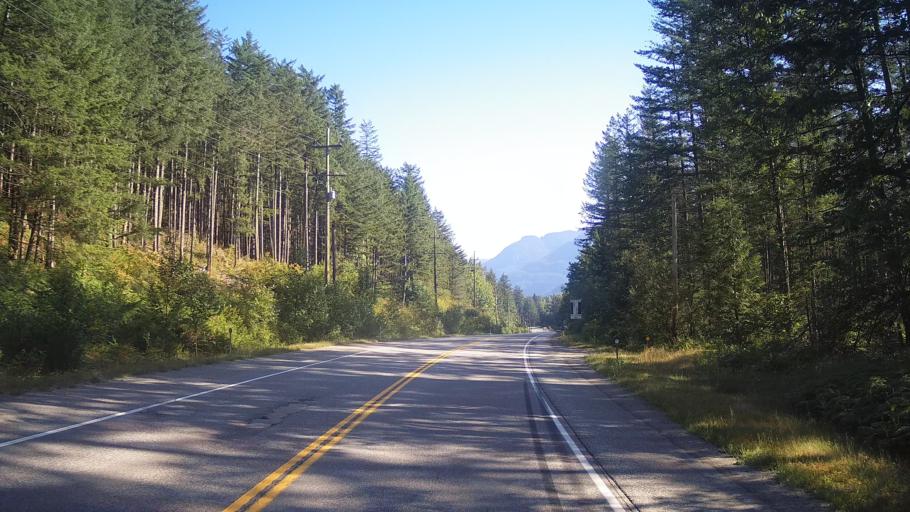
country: CA
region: British Columbia
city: Hope
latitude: 49.4346
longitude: -121.4393
